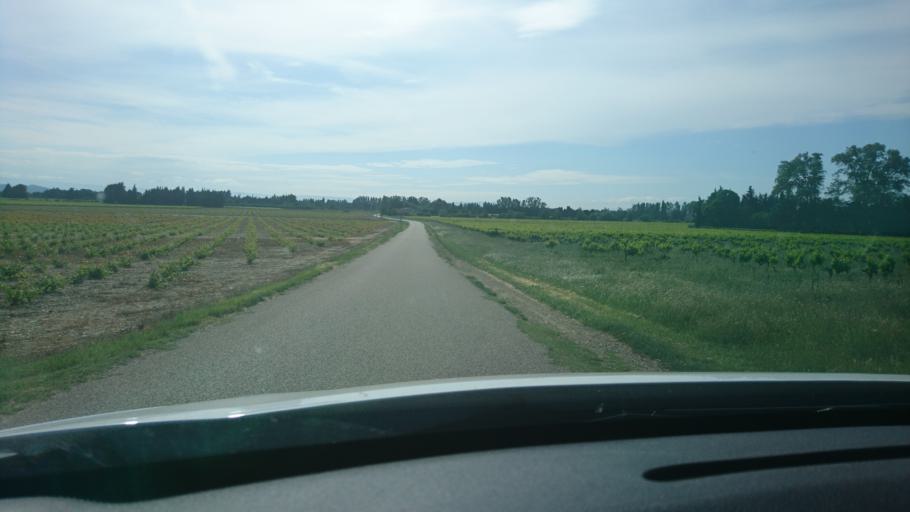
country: FR
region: Provence-Alpes-Cote d'Azur
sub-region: Departement du Vaucluse
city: Jonquieres
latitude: 44.1350
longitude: 4.8797
